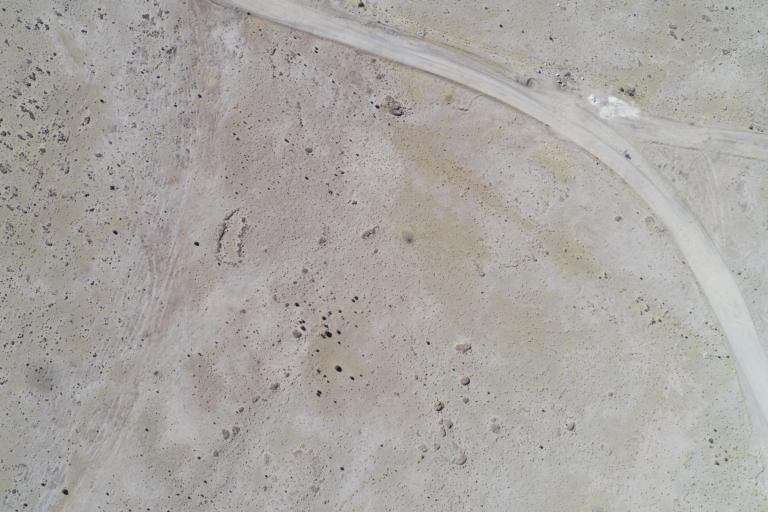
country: BO
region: Potosi
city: Colchani
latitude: -20.3518
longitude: -66.9030
